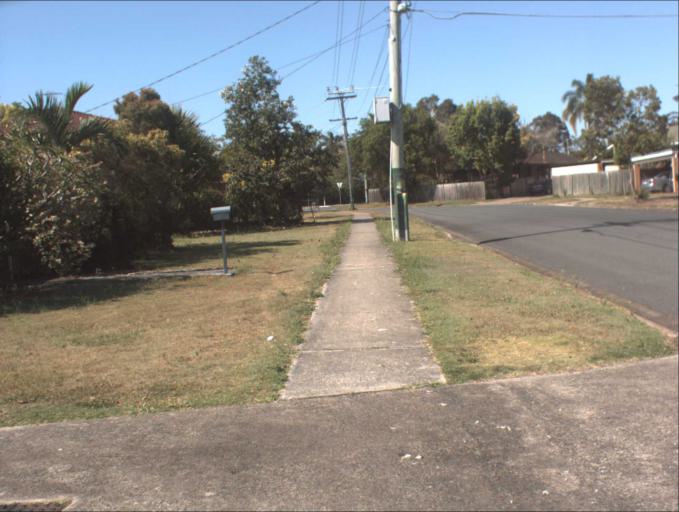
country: AU
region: Queensland
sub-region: Logan
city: Slacks Creek
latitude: -27.6606
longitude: 153.1776
